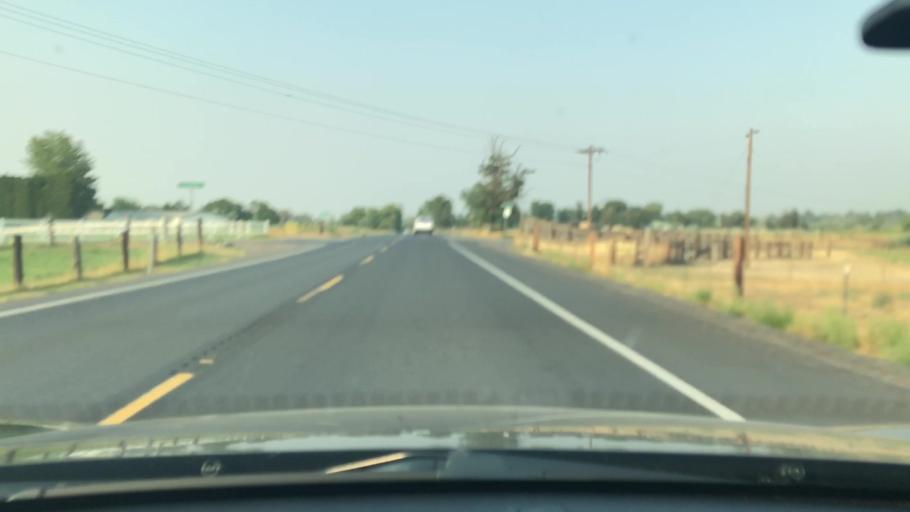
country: US
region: Oregon
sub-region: Umatilla County
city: Hermiston
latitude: 45.8856
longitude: -119.1933
